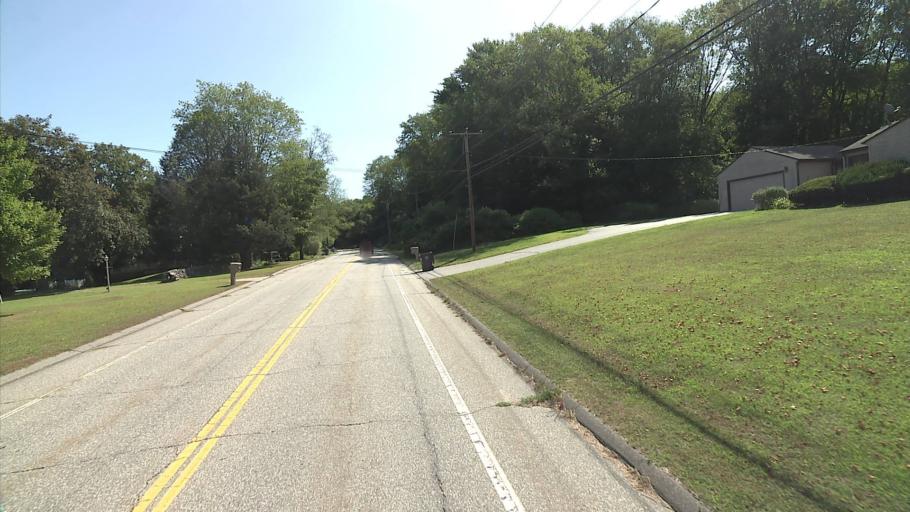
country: US
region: Connecticut
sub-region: New London County
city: Baltic
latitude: 41.6177
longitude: -72.1116
